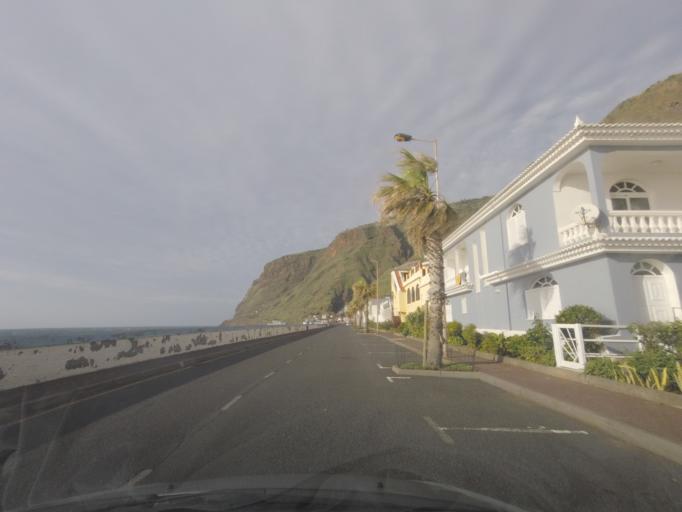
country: PT
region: Madeira
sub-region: Calheta
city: Faja da Ovelha
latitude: 32.7601
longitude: -17.2323
